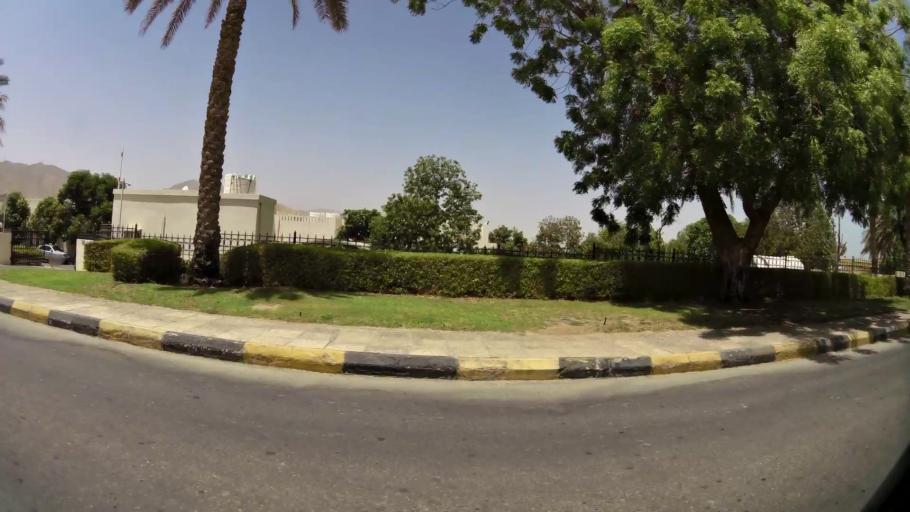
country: OM
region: Muhafazat Masqat
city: Bawshar
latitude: 23.6011
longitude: 58.4701
